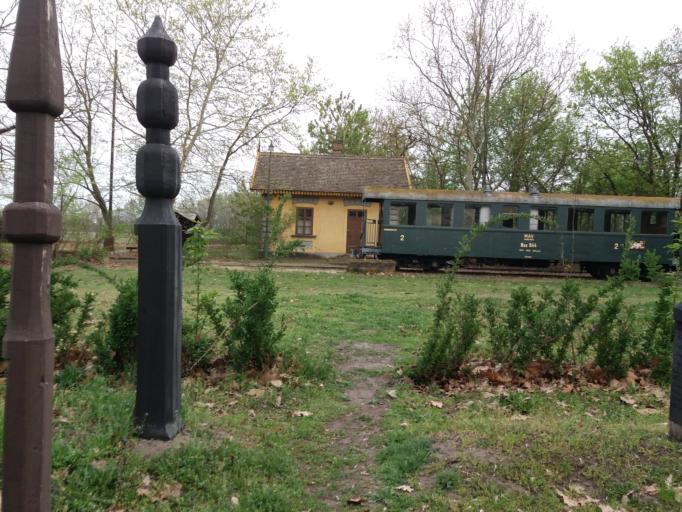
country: HU
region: Csongrad
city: Opusztaszer
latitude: 46.4854
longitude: 20.0967
